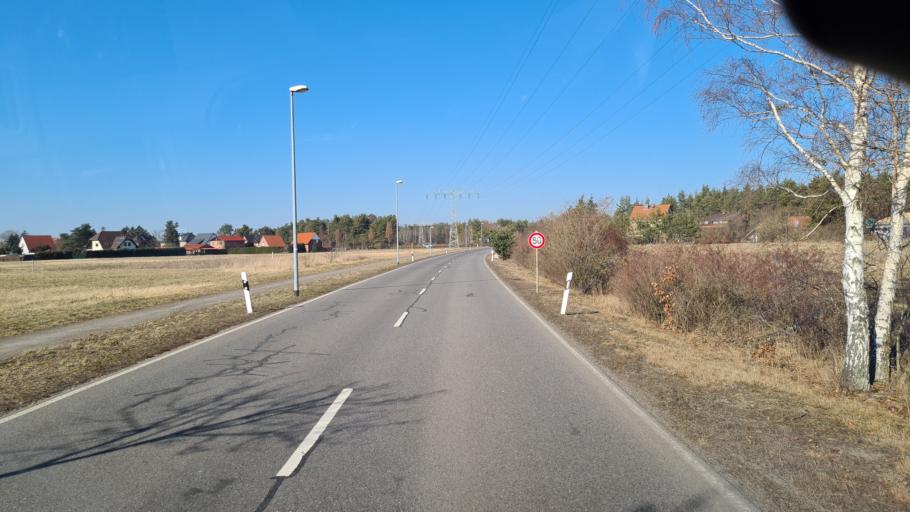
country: DE
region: Brandenburg
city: Grossraschen
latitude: 51.5859
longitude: 14.0311
